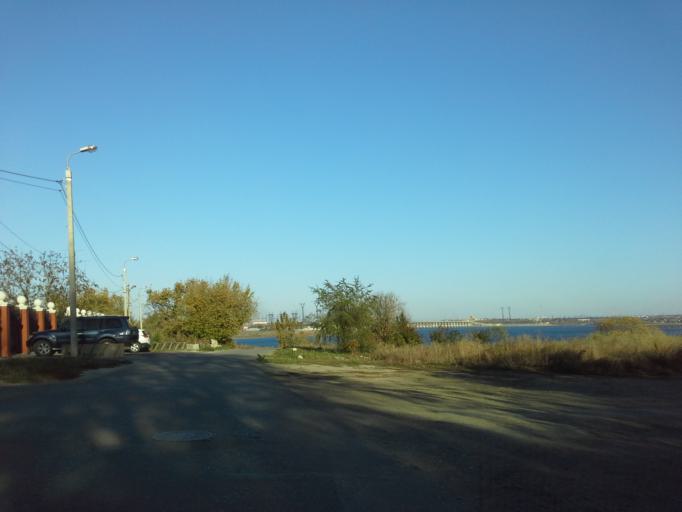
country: RU
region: Volgograd
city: Vodstroy
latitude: 48.8160
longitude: 44.6377
